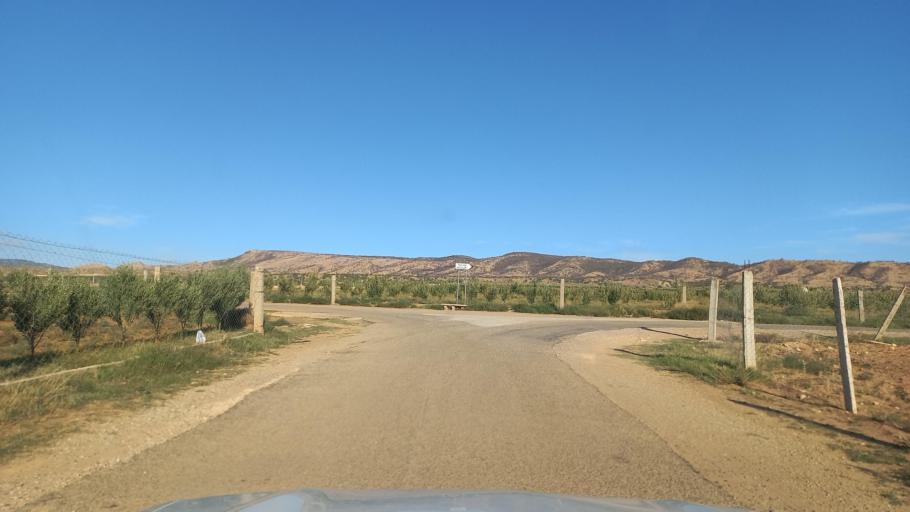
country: TN
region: Al Qasrayn
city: Sbiba
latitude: 35.3372
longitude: 9.1185
